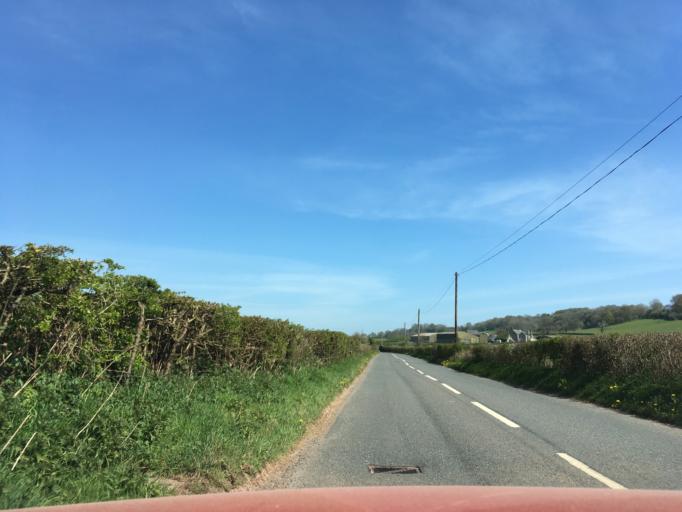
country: GB
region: Wales
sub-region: Monmouthshire
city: Llangwm
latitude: 51.7195
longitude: -2.8414
